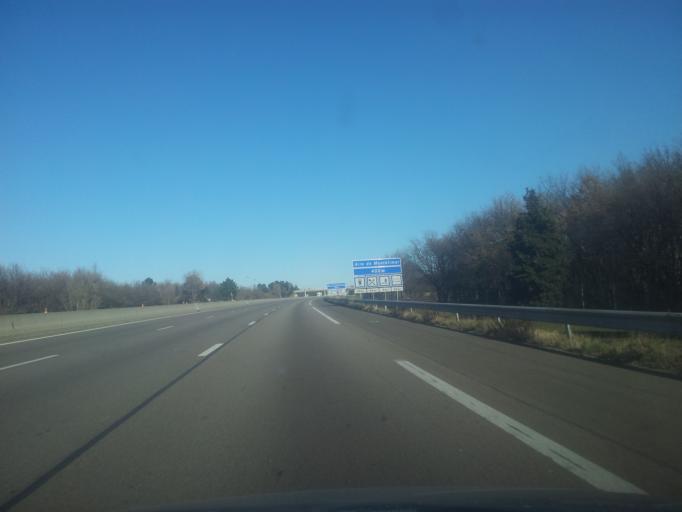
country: FR
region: Rhone-Alpes
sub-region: Departement de la Drome
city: Allan
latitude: 44.5086
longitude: 4.7736
